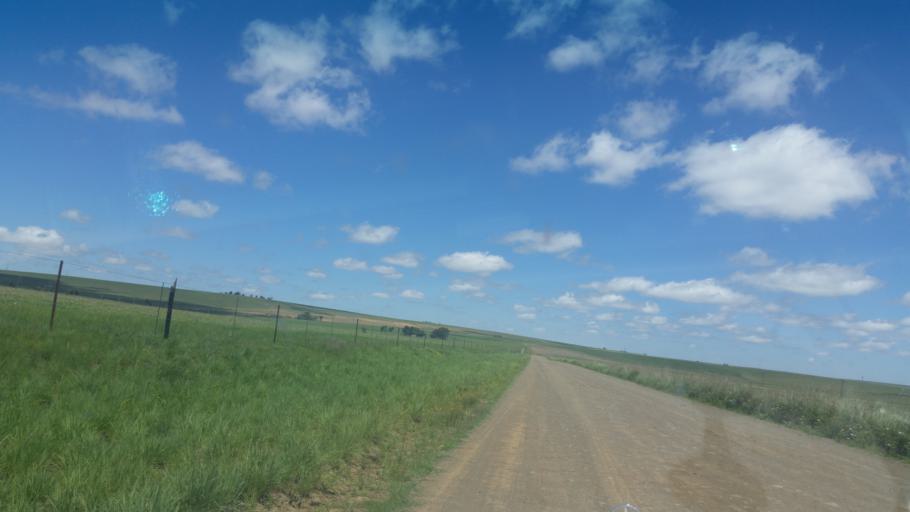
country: ZA
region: Orange Free State
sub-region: Thabo Mofutsanyana District Municipality
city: Harrismith
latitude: -28.2539
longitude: 28.9384
